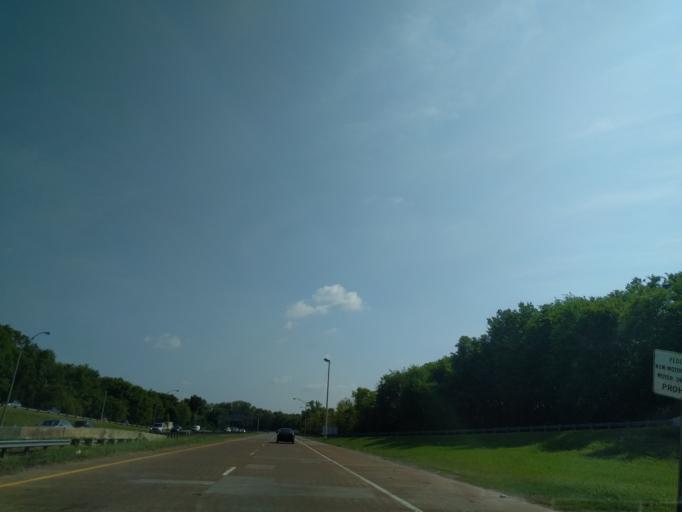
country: US
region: Tennessee
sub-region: Davidson County
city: Nashville
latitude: 36.1761
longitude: -86.7661
